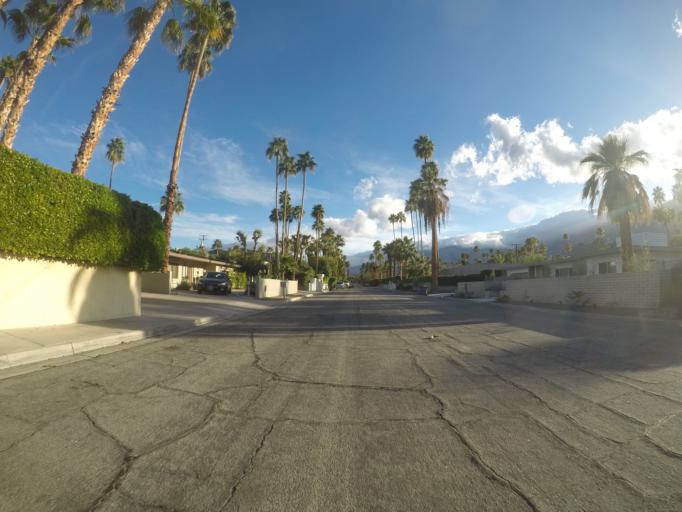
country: US
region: California
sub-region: Riverside County
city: Palm Springs
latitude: 33.8060
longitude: -116.5300
